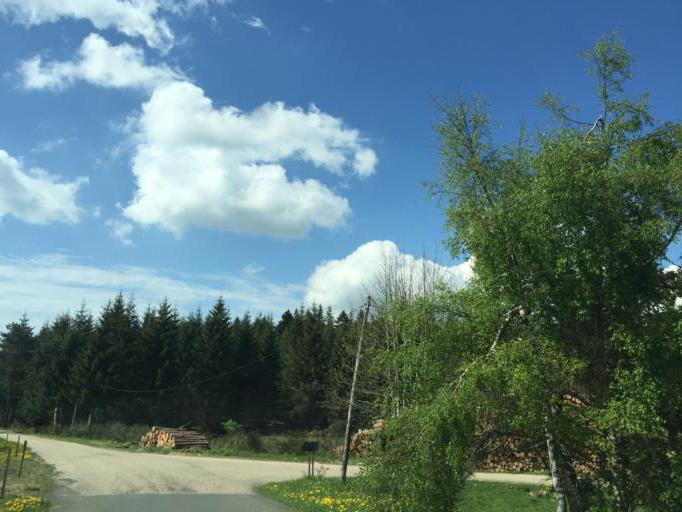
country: FR
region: Rhone-Alpes
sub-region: Departement de la Loire
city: Saint-Sauveur-en-Rue
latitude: 45.2982
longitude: 4.4808
